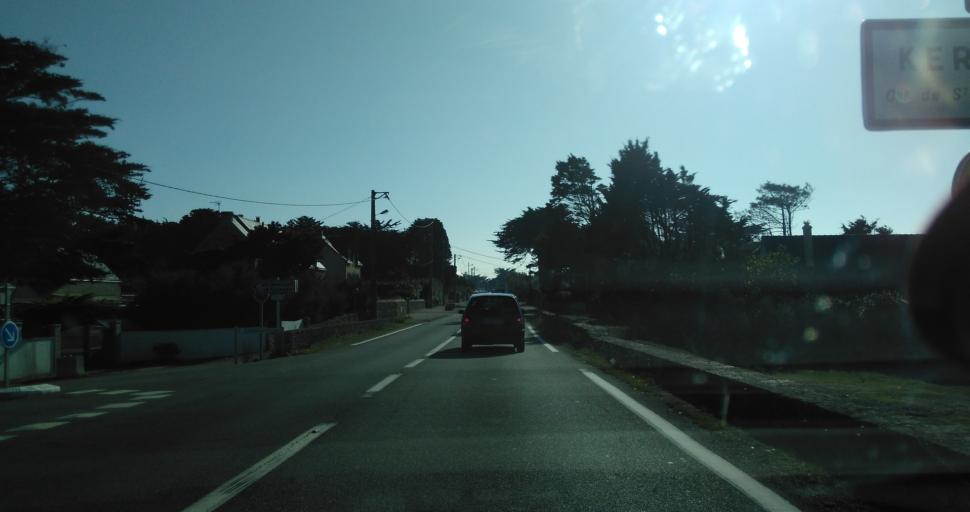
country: FR
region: Brittany
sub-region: Departement du Morbihan
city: Saint-Pierre-Quiberon
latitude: 47.5401
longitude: -3.1351
